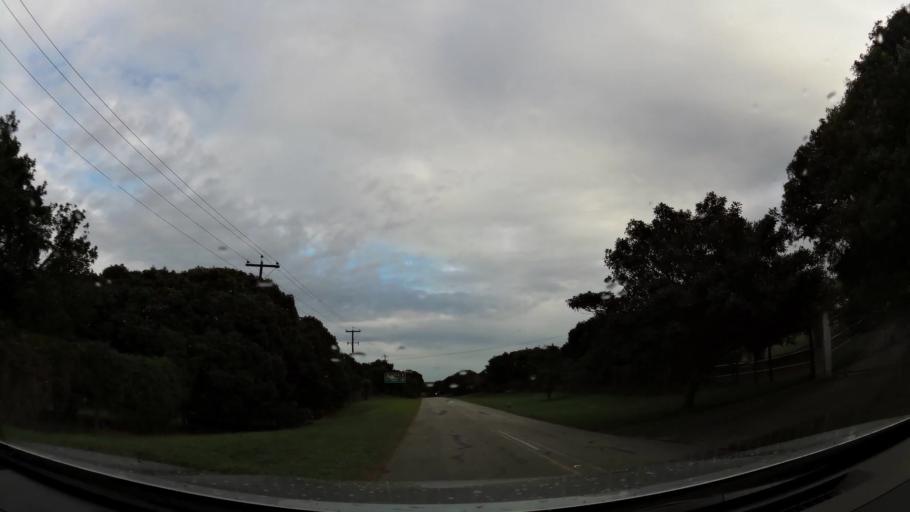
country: ZA
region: Eastern Cape
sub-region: Nelson Mandela Bay Metropolitan Municipality
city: Port Elizabeth
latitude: -34.0168
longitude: 25.5010
